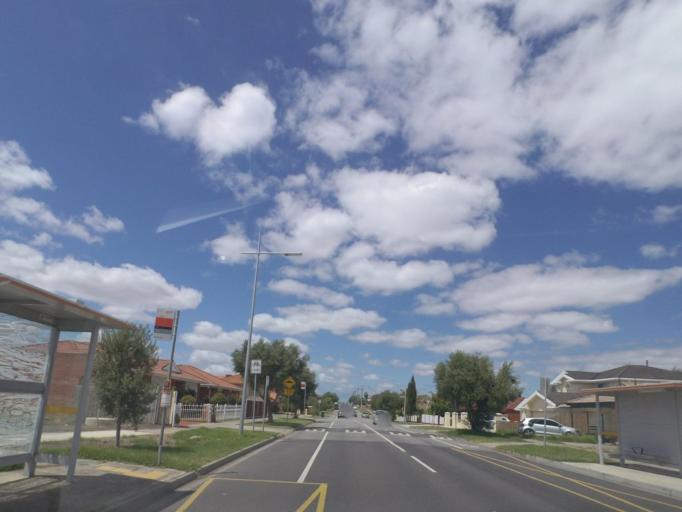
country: AU
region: Victoria
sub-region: Whittlesea
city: Lalor
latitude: -37.6675
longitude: 144.9953
